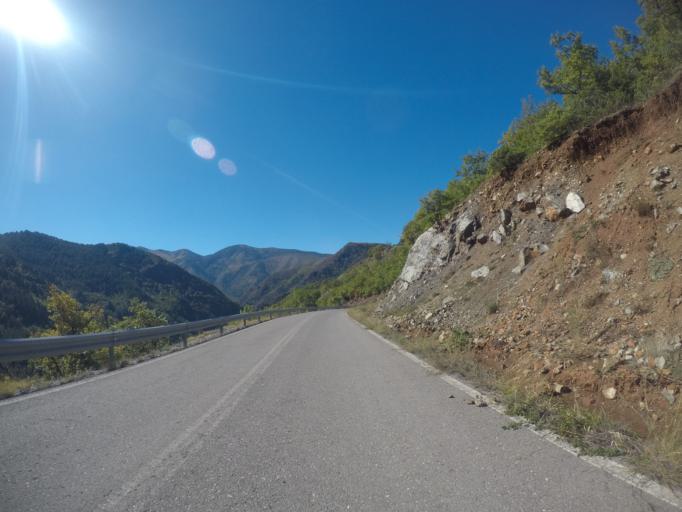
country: GR
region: Epirus
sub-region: Nomos Ioanninon
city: Konitsa
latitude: 40.0305
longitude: 21.0090
